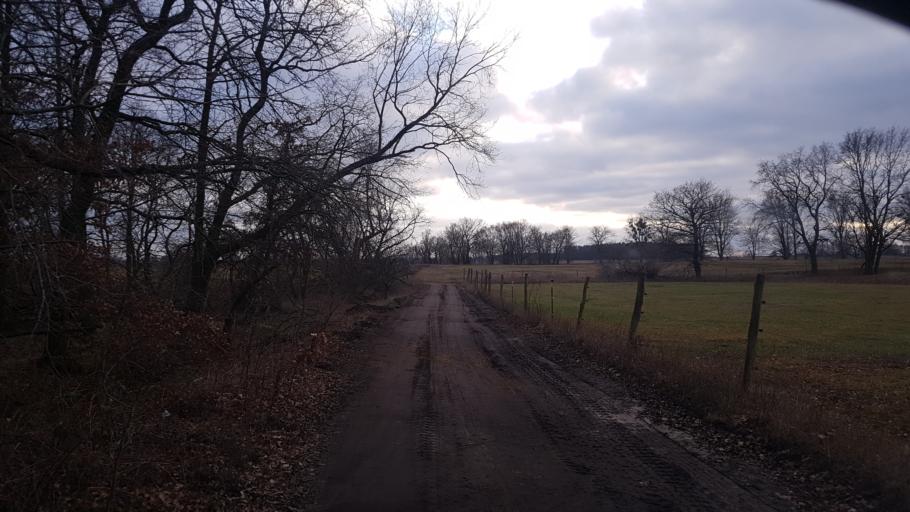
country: DE
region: Brandenburg
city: Ludwigsfelde
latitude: 52.3333
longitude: 13.2223
